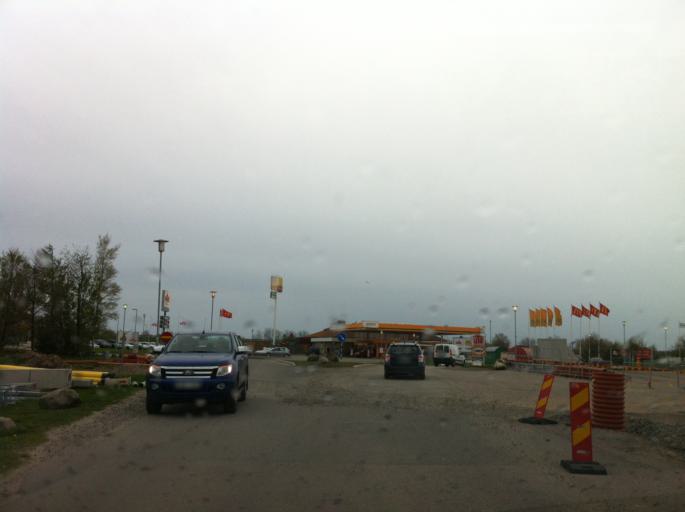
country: SE
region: Halland
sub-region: Falkenbergs Kommun
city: Falkenberg
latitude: 56.9333
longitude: 12.5187
